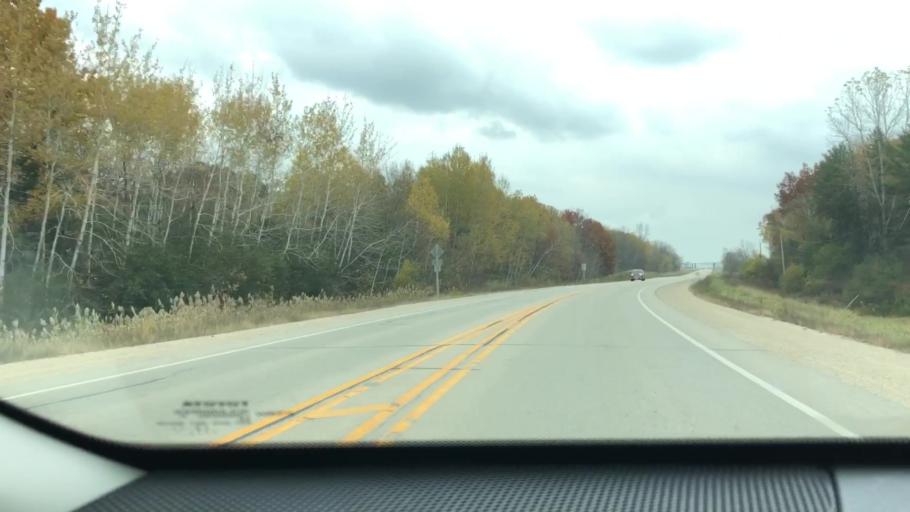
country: US
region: Wisconsin
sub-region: Brown County
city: Oneida
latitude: 44.4994
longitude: -88.1473
